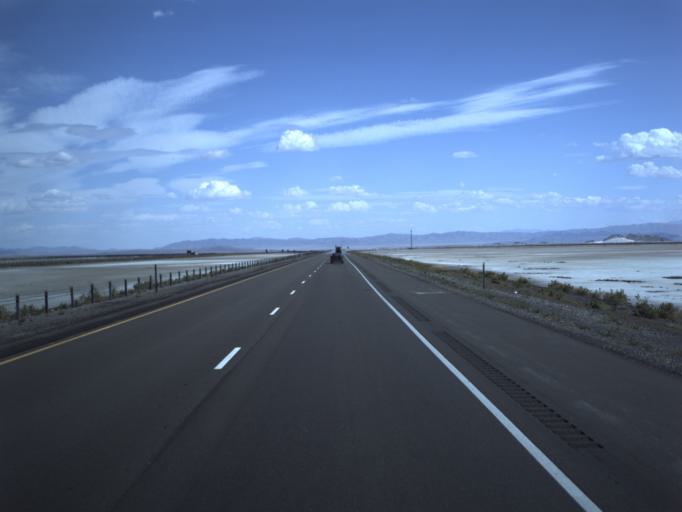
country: US
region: Utah
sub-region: Tooele County
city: Wendover
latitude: 40.7280
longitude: -113.3775
